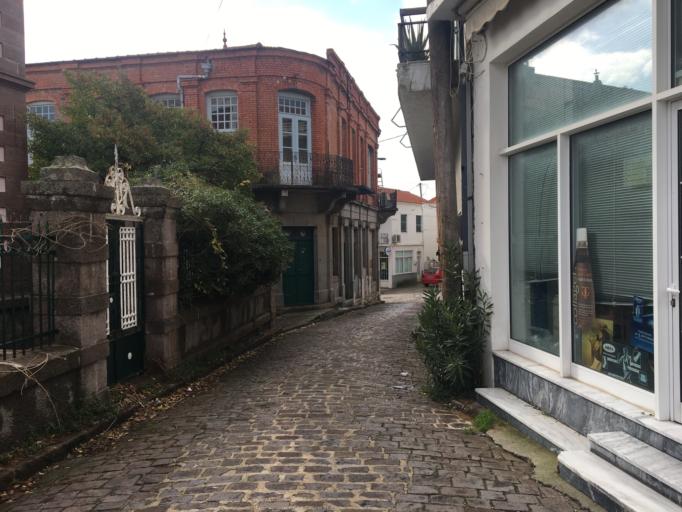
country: GR
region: North Aegean
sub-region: Nomos Lesvou
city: Agia Paraskevi
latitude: 39.2481
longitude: 26.2724
